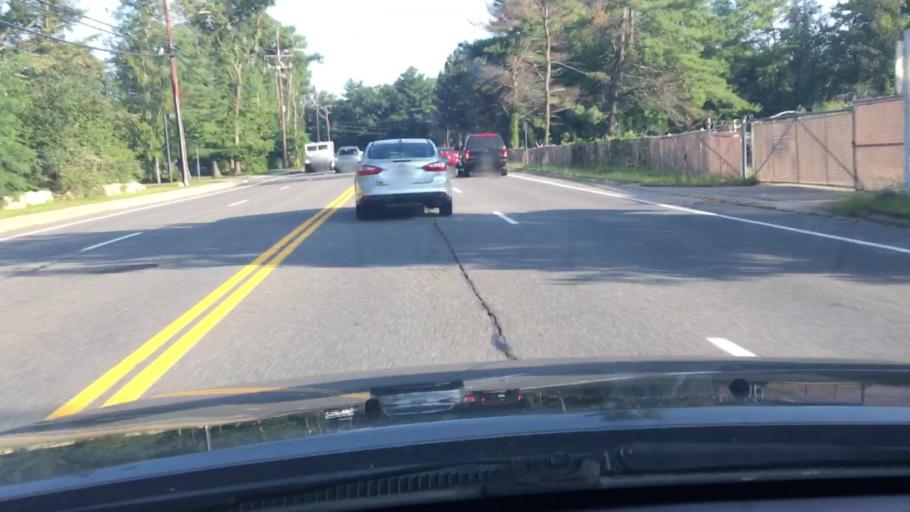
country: US
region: Massachusetts
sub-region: Middlesex County
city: Hopkinton
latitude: 42.2064
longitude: -71.5454
